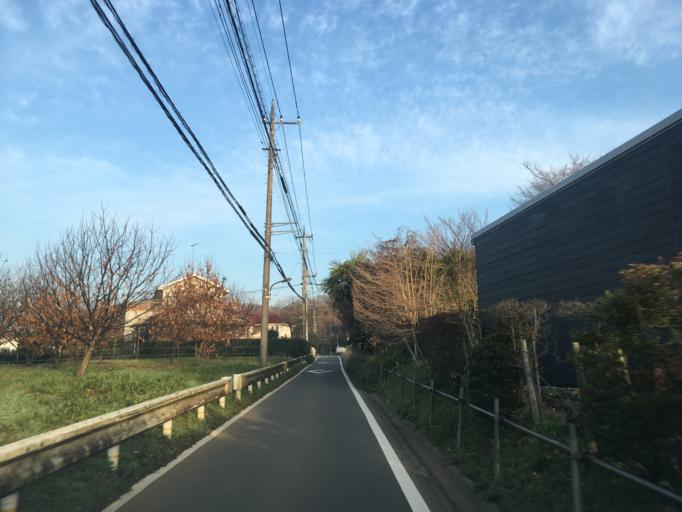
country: JP
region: Tokyo
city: Hino
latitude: 35.6337
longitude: 139.3939
